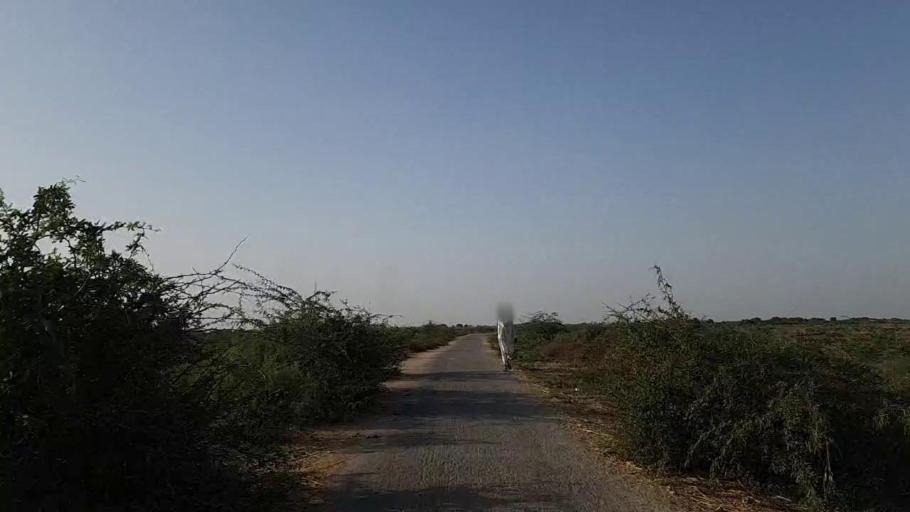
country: PK
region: Sindh
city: Jati
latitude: 24.3052
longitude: 68.1669
